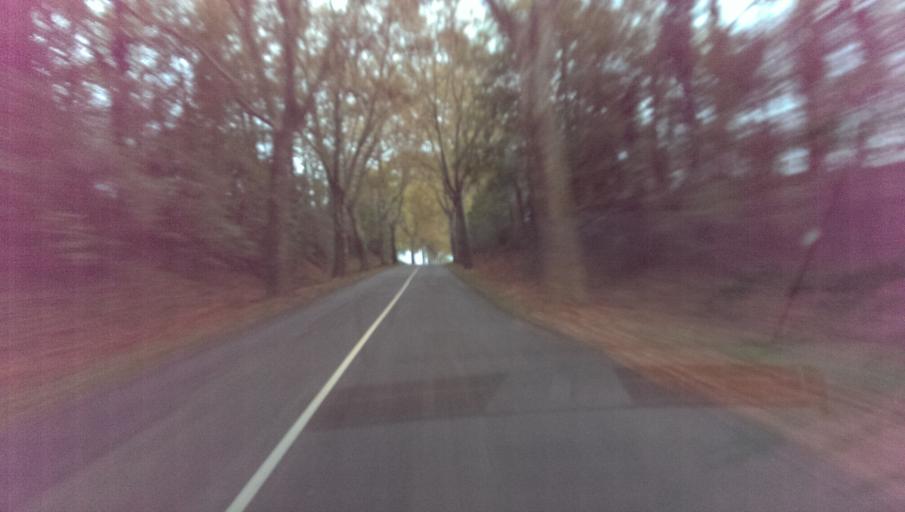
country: DE
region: Rheinland-Pfalz
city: Scheibenhardt
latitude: 48.9490
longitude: 8.1159
